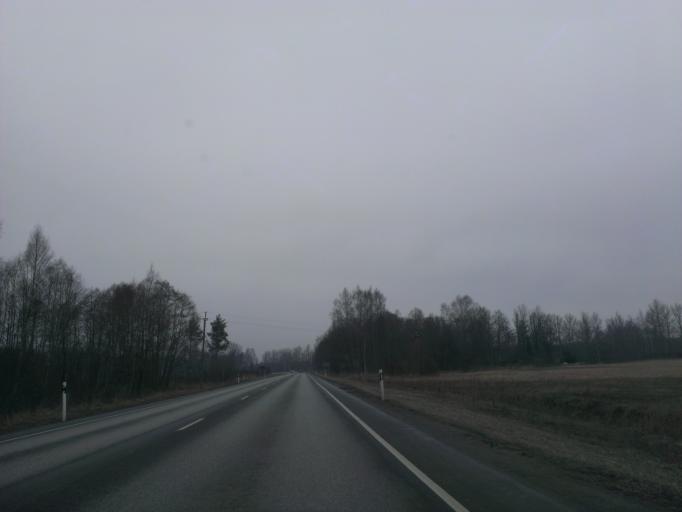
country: EE
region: Paernumaa
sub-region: Audru vald
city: Audru
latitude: 58.4069
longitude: 24.3945
